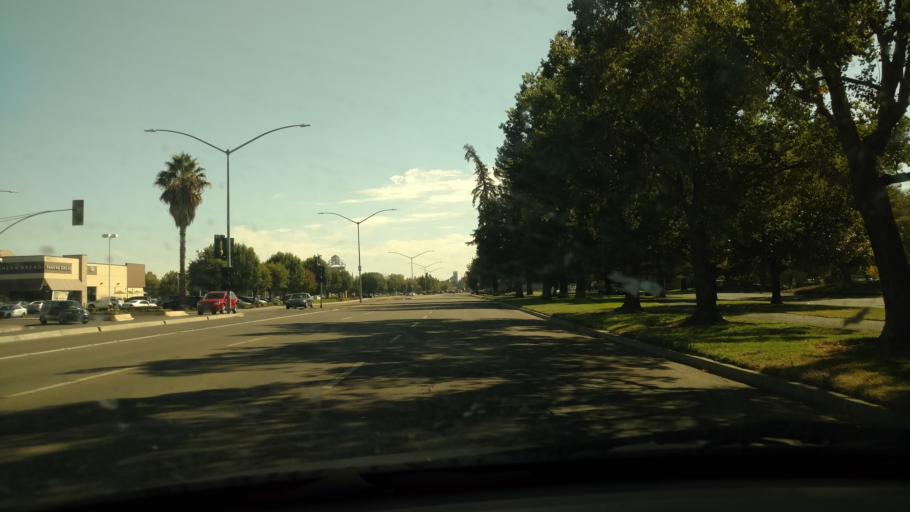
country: US
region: California
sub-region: San Joaquin County
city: Lincoln Village
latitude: 37.9948
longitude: -121.3142
